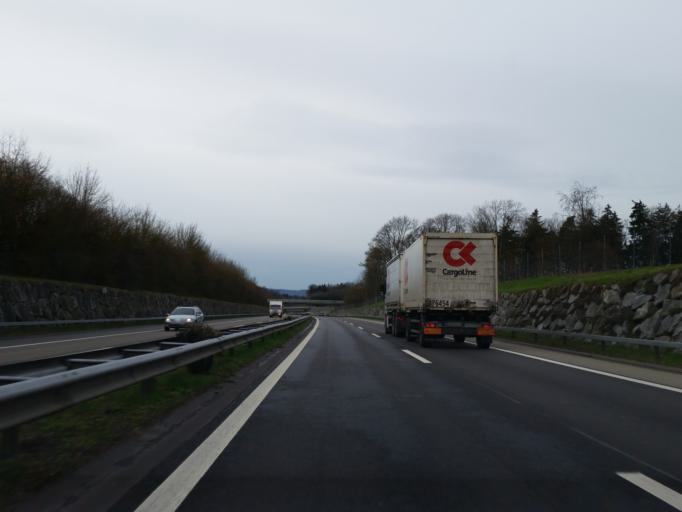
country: CH
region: Thurgau
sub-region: Kreuzlingen District
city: Tagerwilen
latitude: 47.6225
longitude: 9.1180
